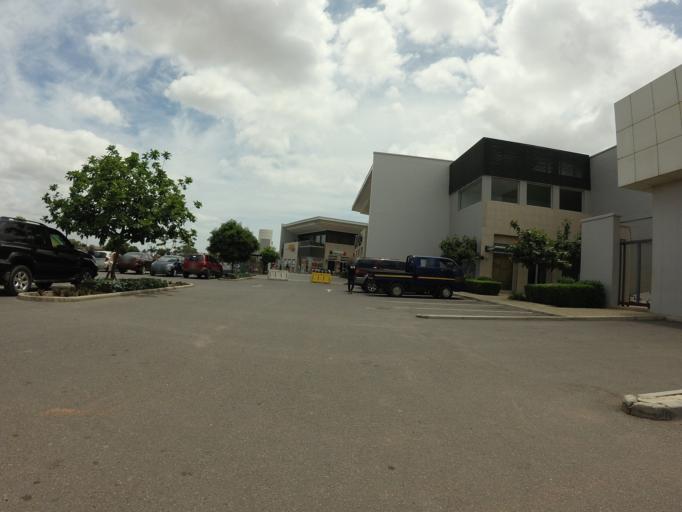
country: GH
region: Greater Accra
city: Gbawe
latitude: 5.5453
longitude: -0.3444
